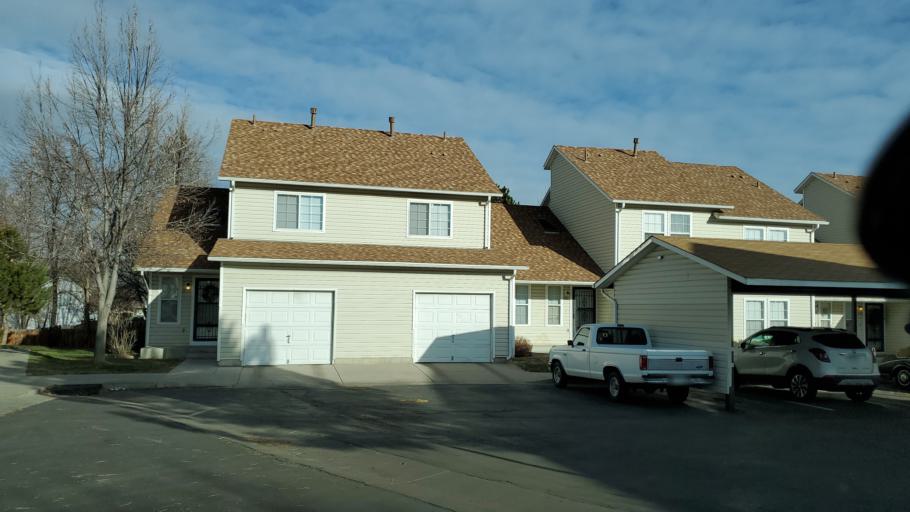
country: US
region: Colorado
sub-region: Adams County
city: Northglenn
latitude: 39.9176
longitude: -104.9431
